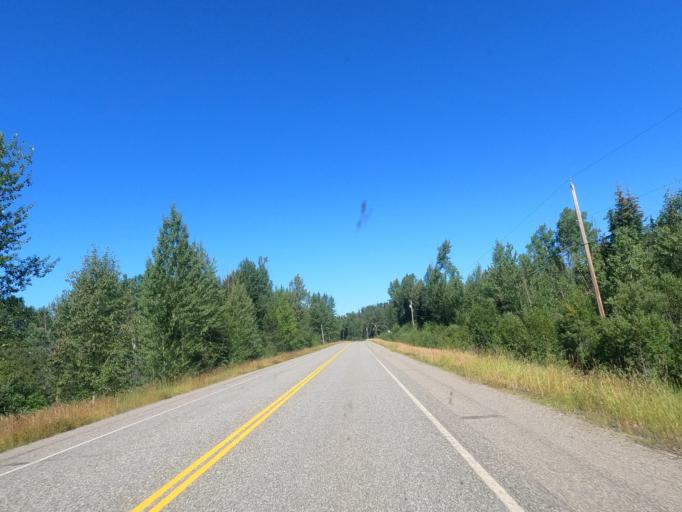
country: CA
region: British Columbia
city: Quesnel
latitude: 53.0394
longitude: -122.1368
